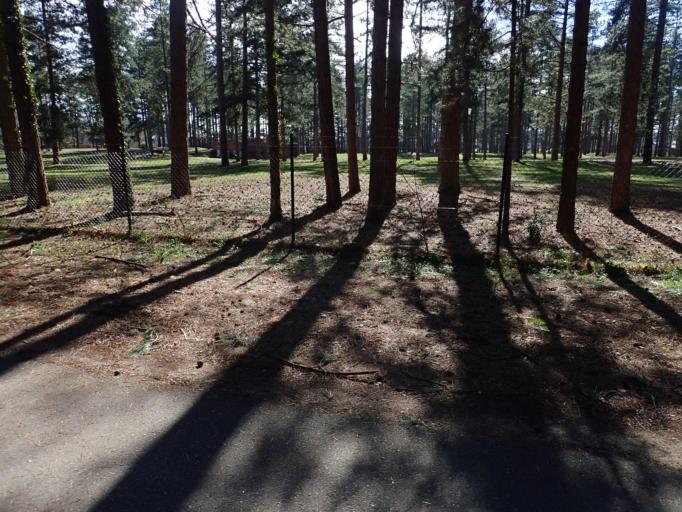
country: BE
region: Flanders
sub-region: Provincie Vlaams-Brabant
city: Scherpenheuvel-Zichem
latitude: 51.0267
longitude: 4.9943
